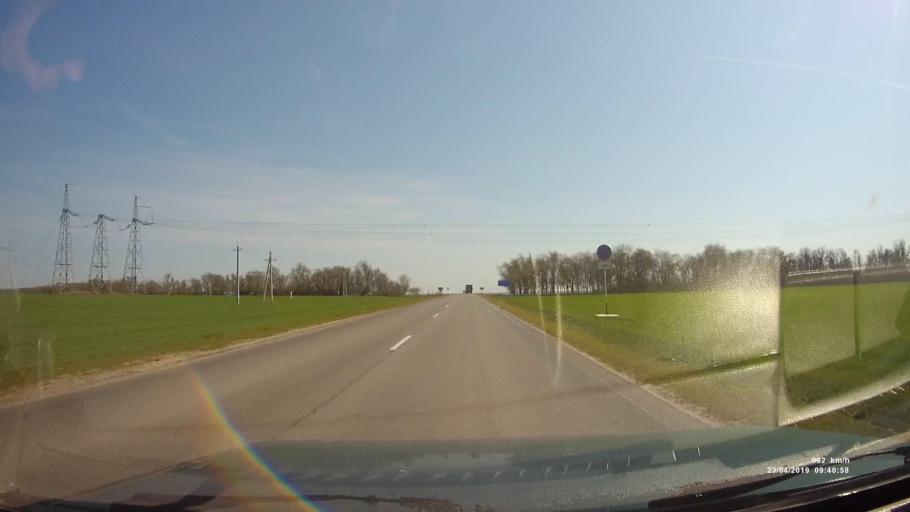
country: RU
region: Rostov
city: Gundorovskiy
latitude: 46.8622
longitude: 41.9531
